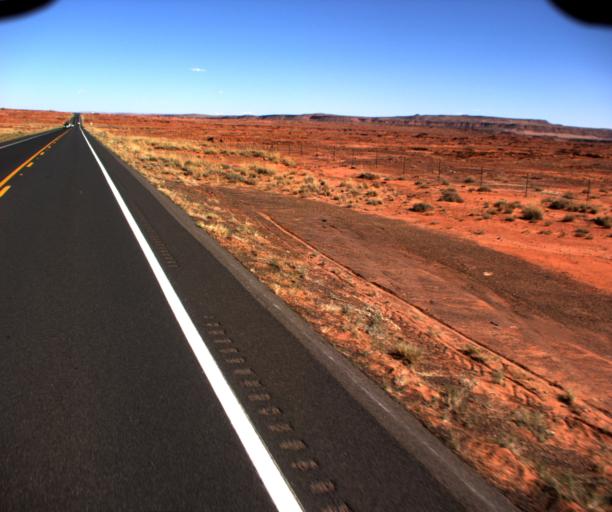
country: US
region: Arizona
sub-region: Coconino County
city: Tuba City
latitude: 36.0992
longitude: -111.3347
